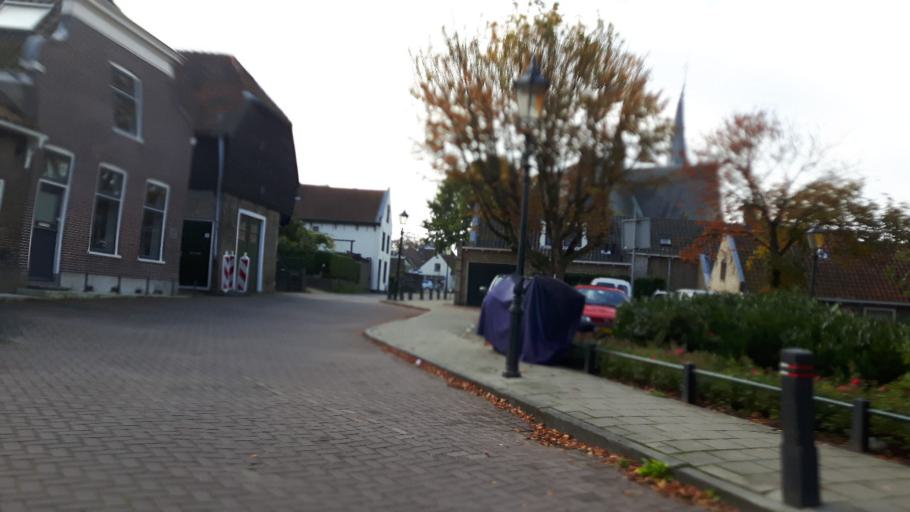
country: NL
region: South Holland
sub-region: Gemeente Gouda
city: Gouda
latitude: 51.9871
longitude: 4.6724
